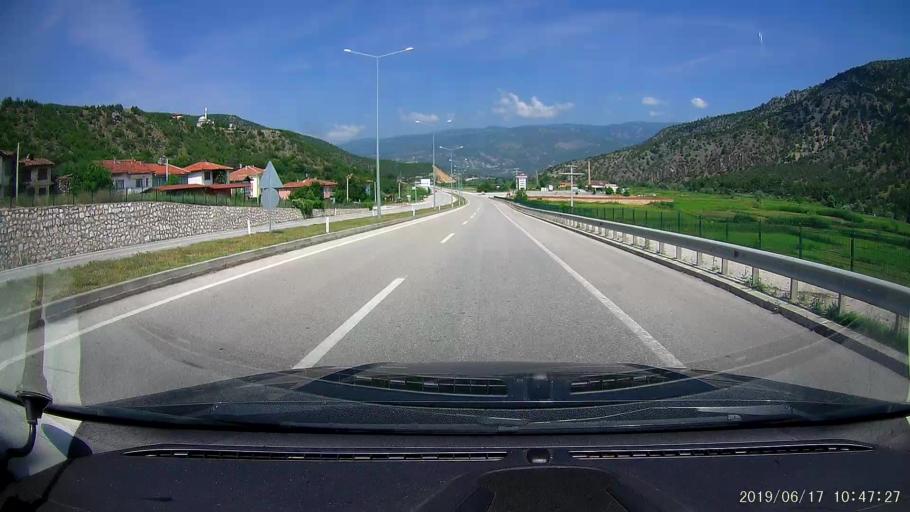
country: TR
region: Corum
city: Hacihamza
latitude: 41.0773
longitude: 34.4489
